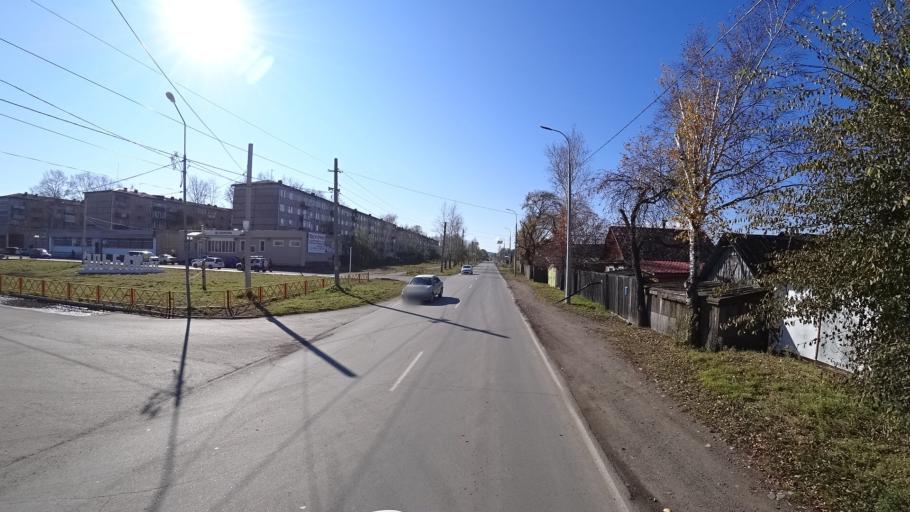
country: RU
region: Khabarovsk Krai
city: Amursk
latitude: 50.1012
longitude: 136.5101
